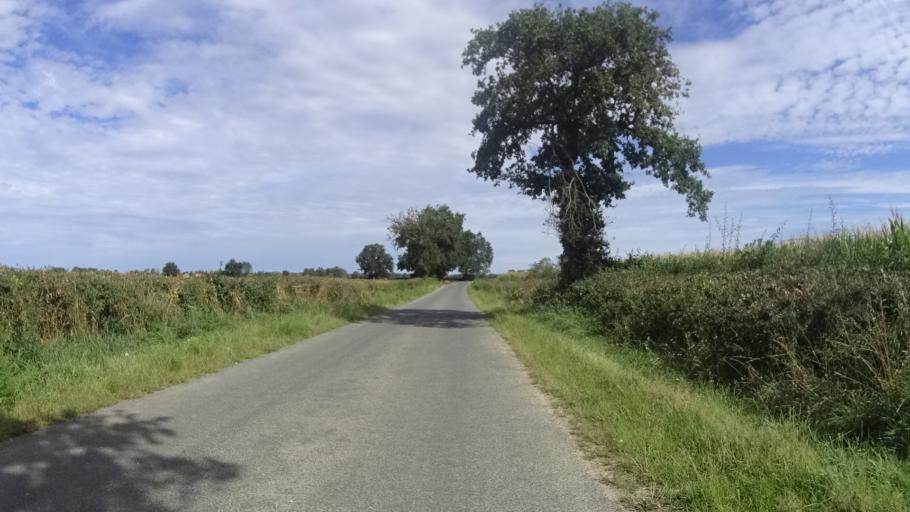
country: FR
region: Auvergne
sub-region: Departement de l'Allier
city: Beaulon
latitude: 46.6367
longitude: 3.6942
